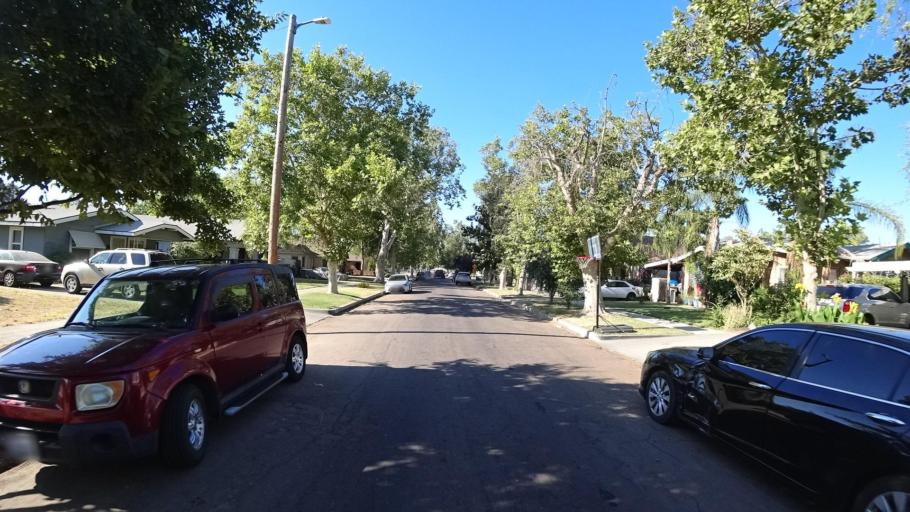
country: US
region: California
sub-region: Fresno County
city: Fresno
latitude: 36.7553
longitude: -119.8154
